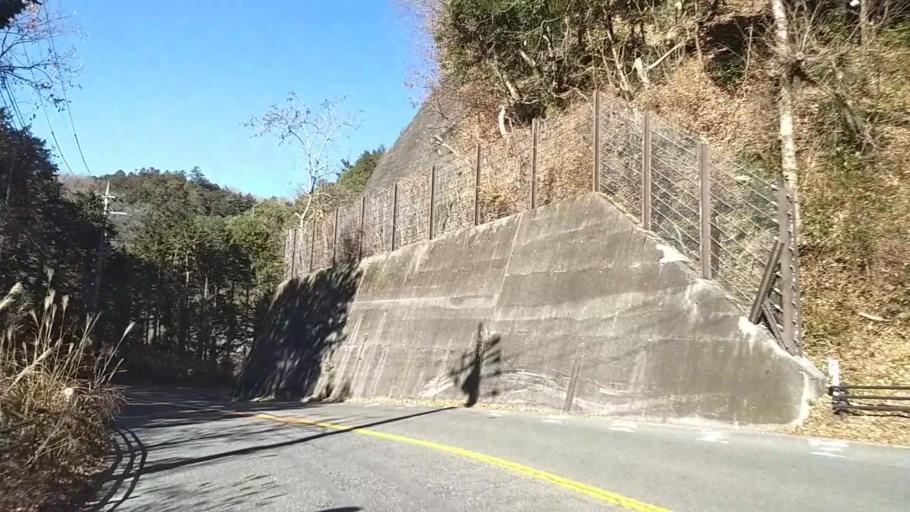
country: JP
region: Yamanashi
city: Uenohara
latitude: 35.6172
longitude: 139.2151
